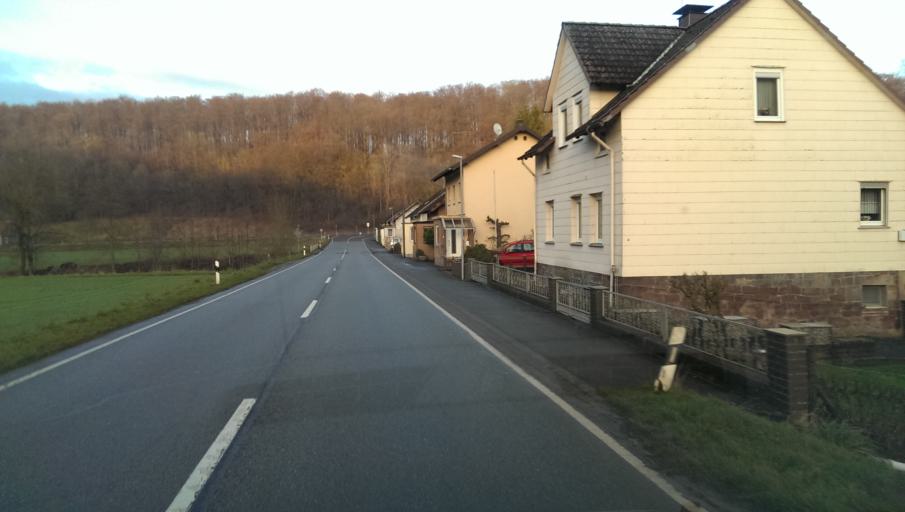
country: DE
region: Lower Saxony
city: Lenne
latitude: 51.9021
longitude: 9.6833
